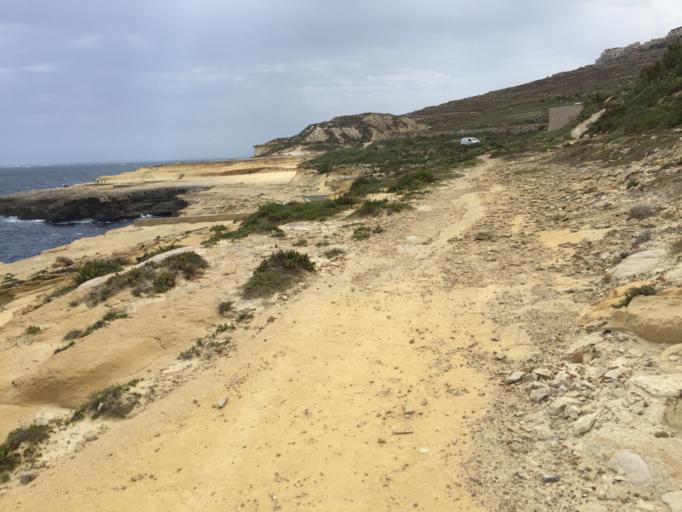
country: MT
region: Iz-Zebbug
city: Zebbug
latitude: 36.0810
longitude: 14.2329
